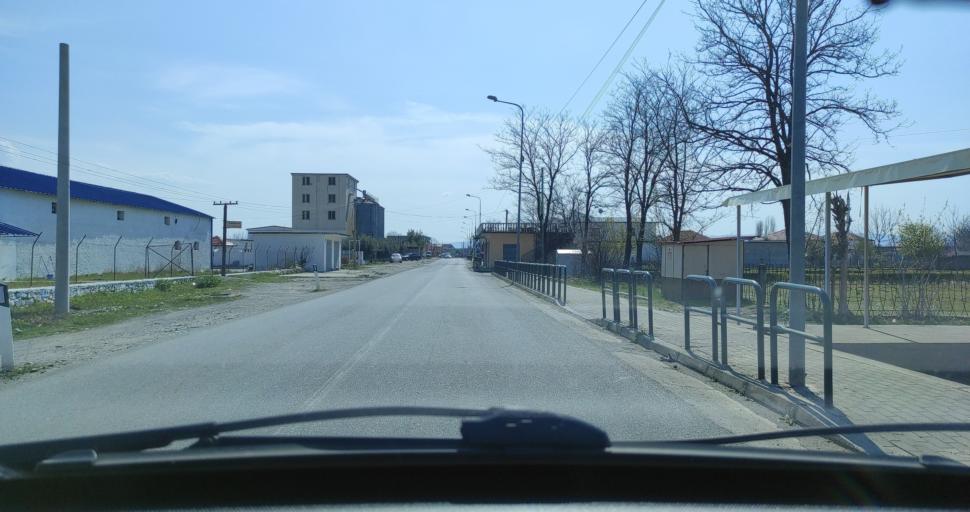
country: AL
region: Shkoder
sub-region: Rrethi i Shkodres
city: Vau i Dejes
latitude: 42.0046
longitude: 19.6179
